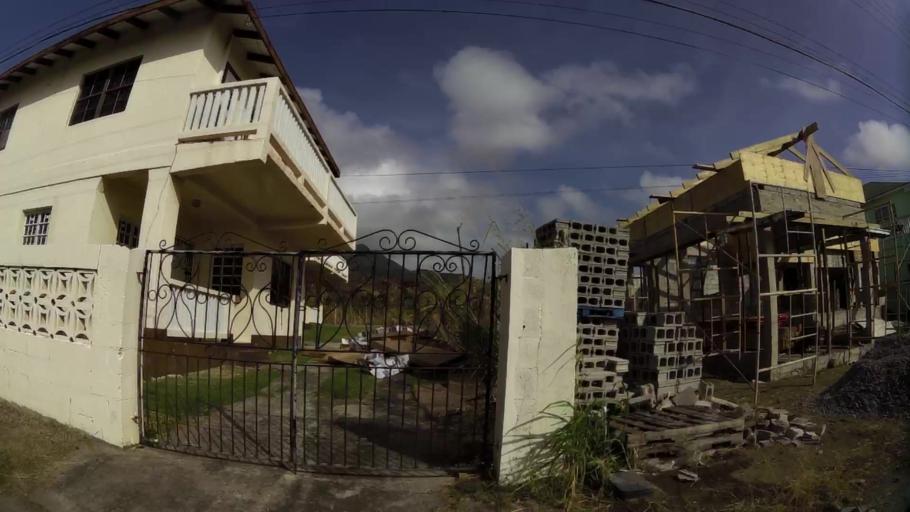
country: KN
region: Saint George Basseterre
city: Basseterre
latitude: 17.2972
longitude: -62.7414
